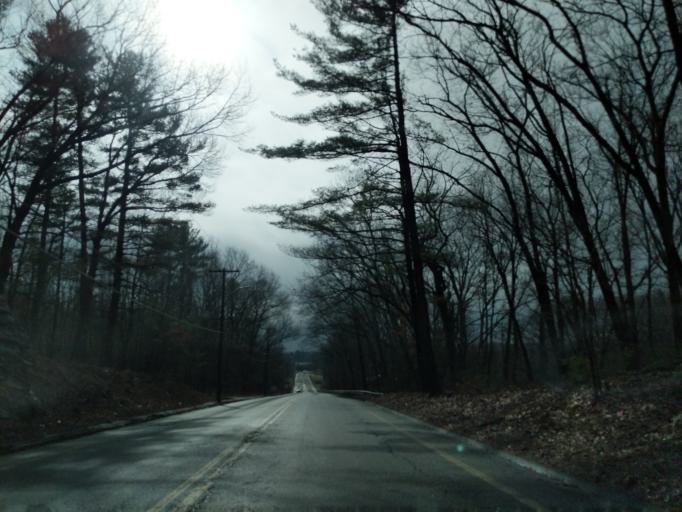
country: US
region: Massachusetts
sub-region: Worcester County
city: Webster
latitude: 42.0694
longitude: -71.8660
